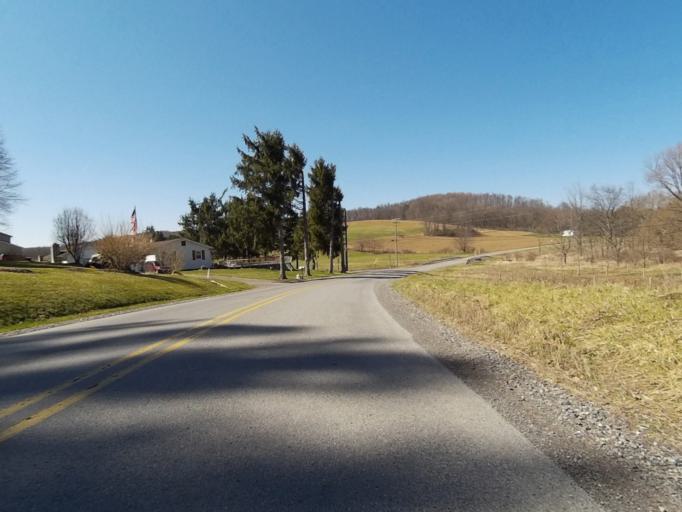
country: US
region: Pennsylvania
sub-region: Centre County
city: Stormstown
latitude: 40.7530
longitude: -78.0371
